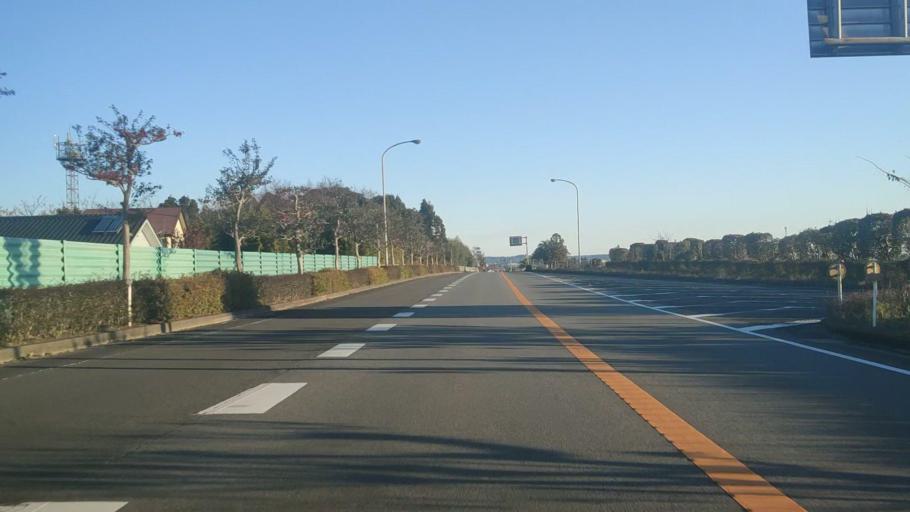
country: JP
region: Miyazaki
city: Tsuma
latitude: 32.0375
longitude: 131.4670
